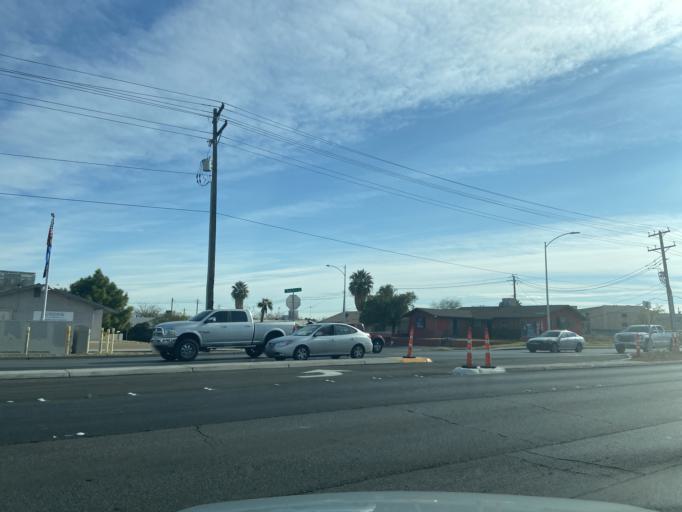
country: US
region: Nevada
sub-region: Clark County
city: North Las Vegas
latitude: 36.1799
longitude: -115.1162
